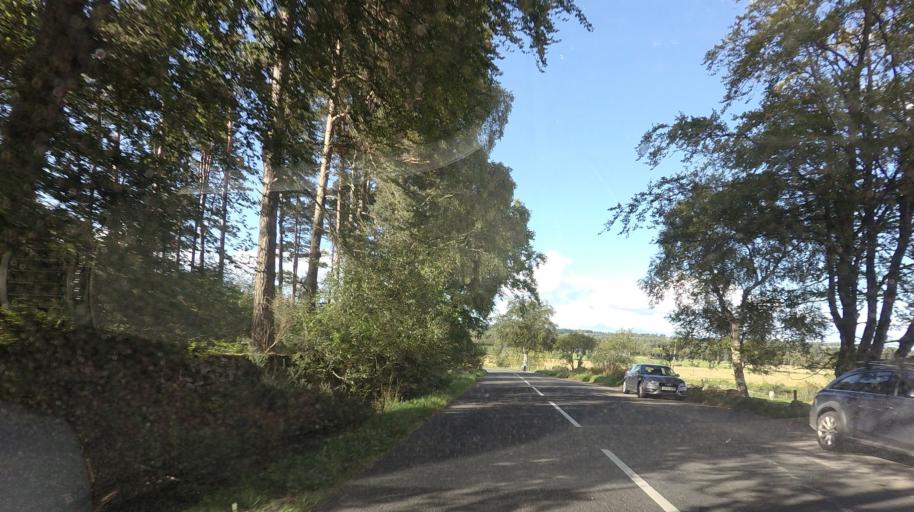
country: GB
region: Scotland
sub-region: Aberdeenshire
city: Banchory
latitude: 57.1248
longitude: -2.4259
